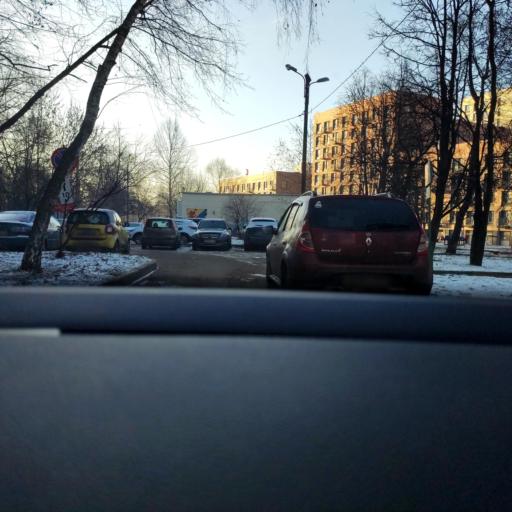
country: RU
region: Moscow
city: Metrogorodok
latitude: 55.7972
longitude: 37.7679
